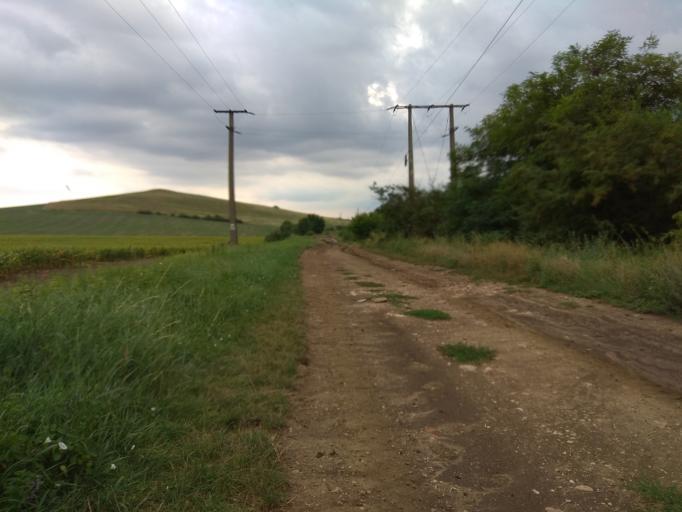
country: HU
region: Borsod-Abauj-Zemplen
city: Monok
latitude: 48.1863
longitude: 21.1258
